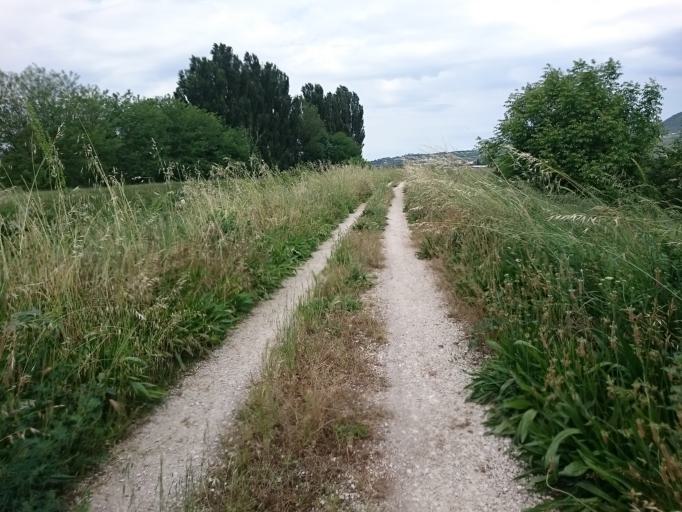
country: IT
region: Veneto
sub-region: Provincia di Padova
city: Baone
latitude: 45.2187
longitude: 11.6957
